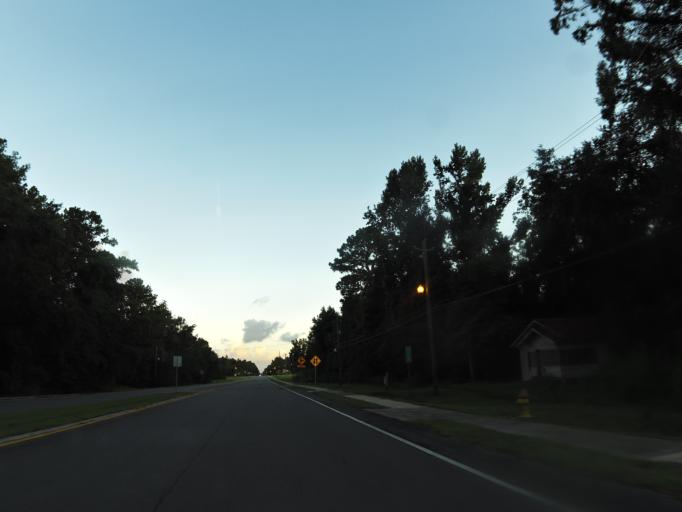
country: US
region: Georgia
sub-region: Camden County
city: Woodbine
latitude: 30.9563
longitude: -81.7214
